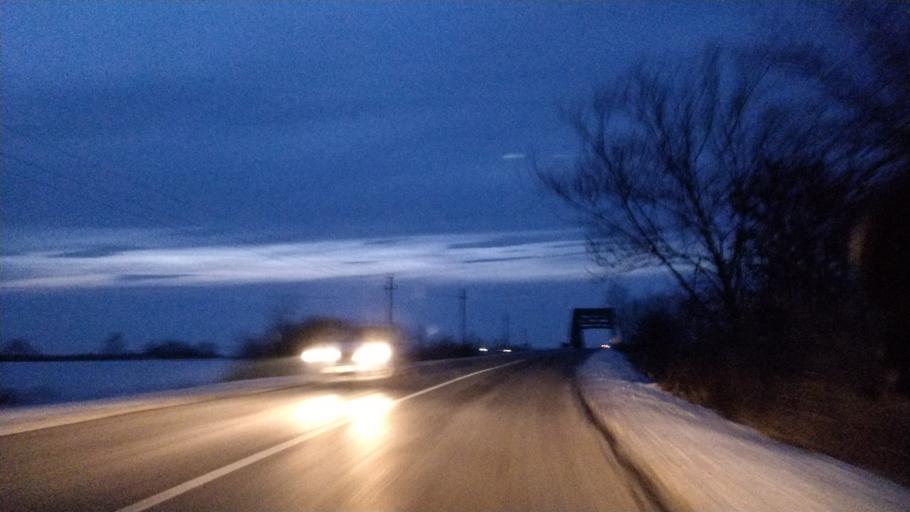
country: RO
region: Vrancea
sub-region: Comuna Rastoaca
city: Rastoaca
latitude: 45.6487
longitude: 27.3191
